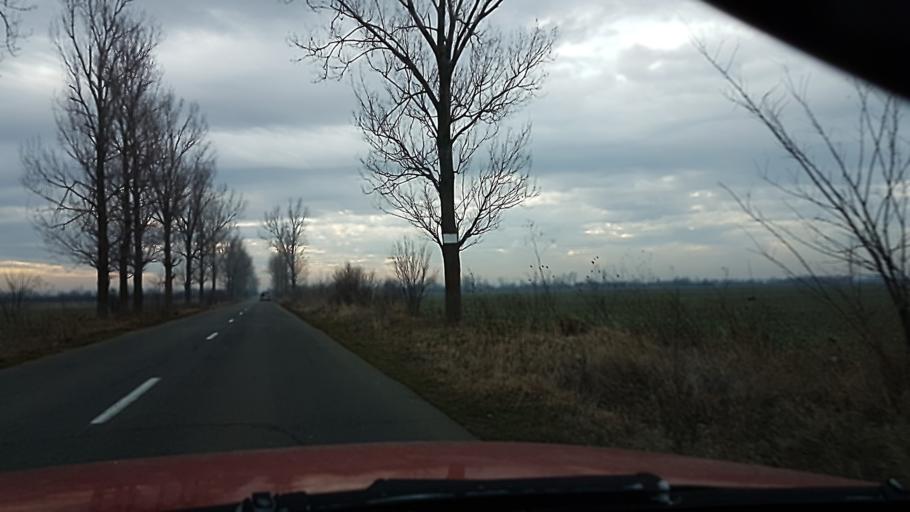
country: RO
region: Giurgiu
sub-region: Comuna Herasti
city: Herasti
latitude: 44.2269
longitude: 26.3609
